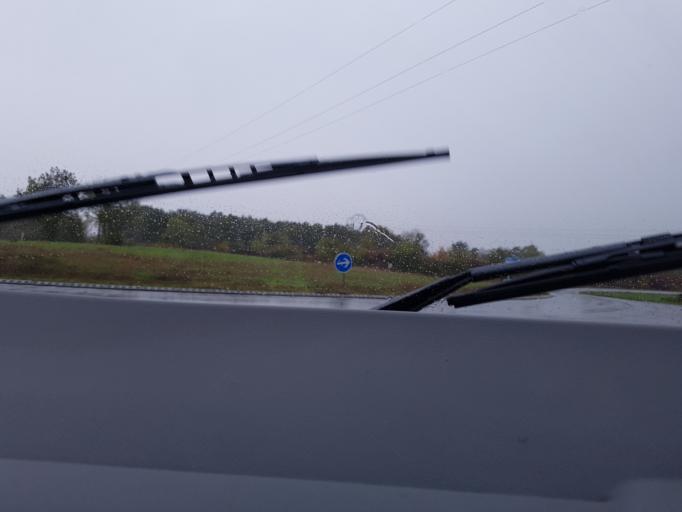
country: FR
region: Aquitaine
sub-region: Departement de la Gironde
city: Saint-Louis-de-Montferrand
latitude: 44.9601
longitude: -0.5179
